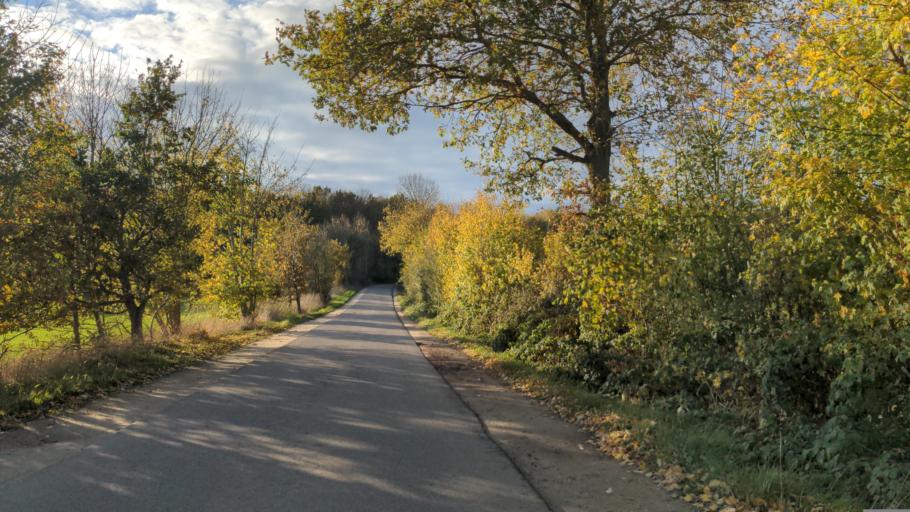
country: DE
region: Schleswig-Holstein
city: Wesenberg
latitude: 53.8419
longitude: 10.5329
